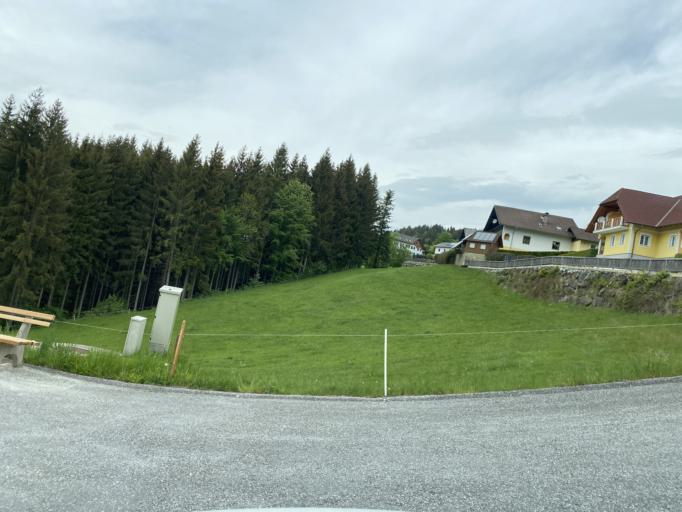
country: AT
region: Styria
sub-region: Politischer Bezirk Weiz
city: Gschaid bei Birkfeld
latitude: 47.3462
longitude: 15.7340
